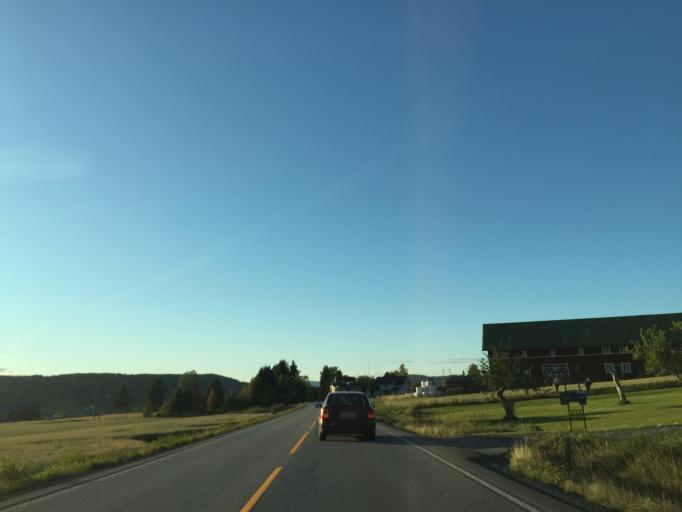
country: NO
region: Hedmark
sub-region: Nord-Odal
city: Sand
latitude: 60.4144
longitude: 11.5159
